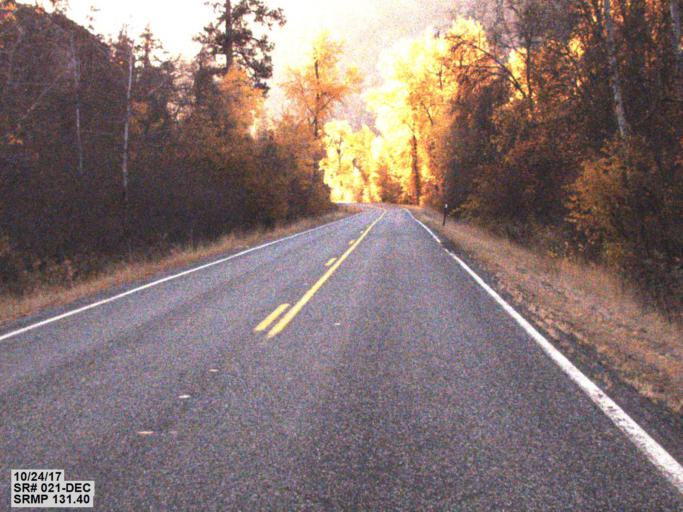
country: US
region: Washington
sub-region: Ferry County
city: Republic
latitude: 48.2731
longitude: -118.7130
